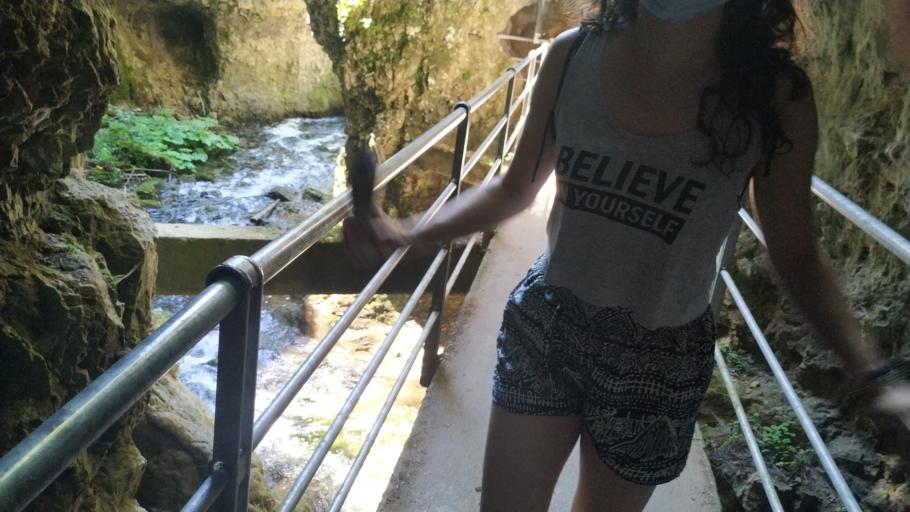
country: IT
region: Trentino-Alto Adige
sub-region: Provincia di Trento
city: Fondo
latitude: 46.4434
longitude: 11.1419
